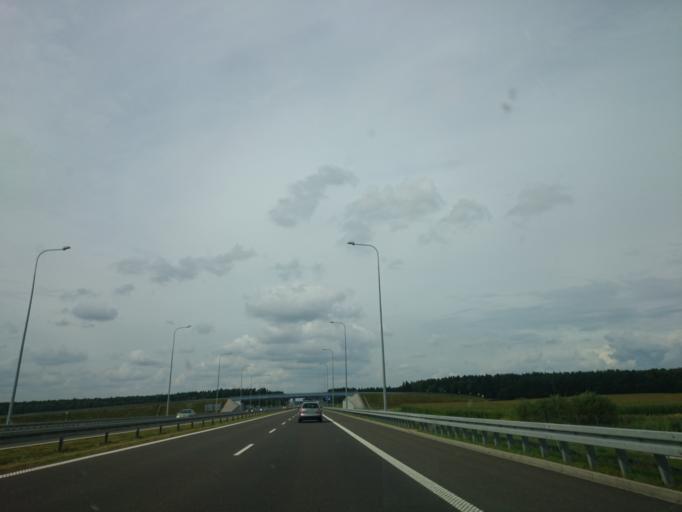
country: PL
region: West Pomeranian Voivodeship
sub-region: Powiat pyrzycki
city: Bielice
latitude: 53.1469
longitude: 14.7165
